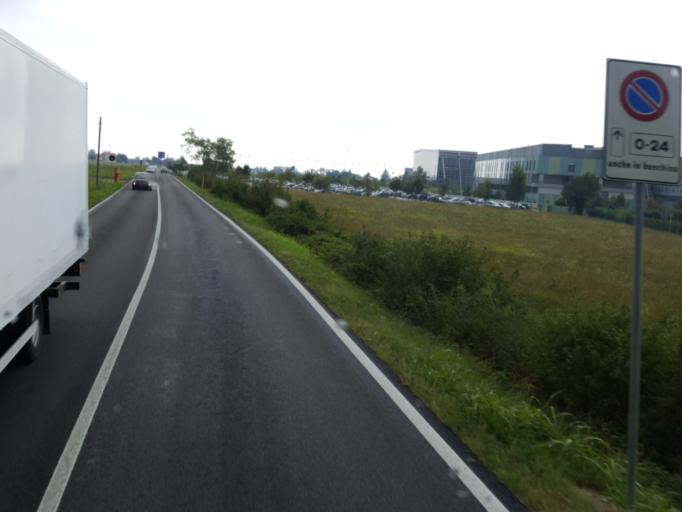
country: IT
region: Veneto
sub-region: Provincia di Vicenza
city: Santorso
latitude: 45.7300
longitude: 11.4130
